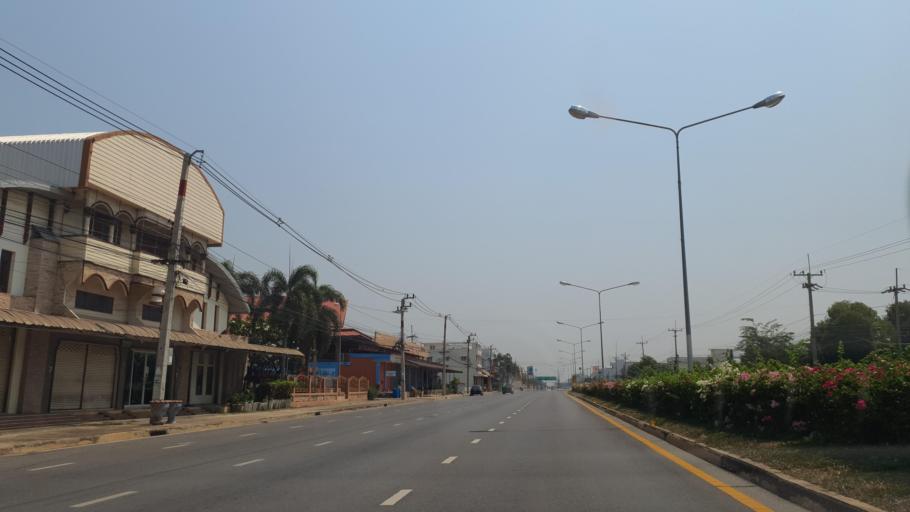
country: TH
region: Suphan Buri
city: U Thong
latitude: 14.2493
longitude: 99.8147
